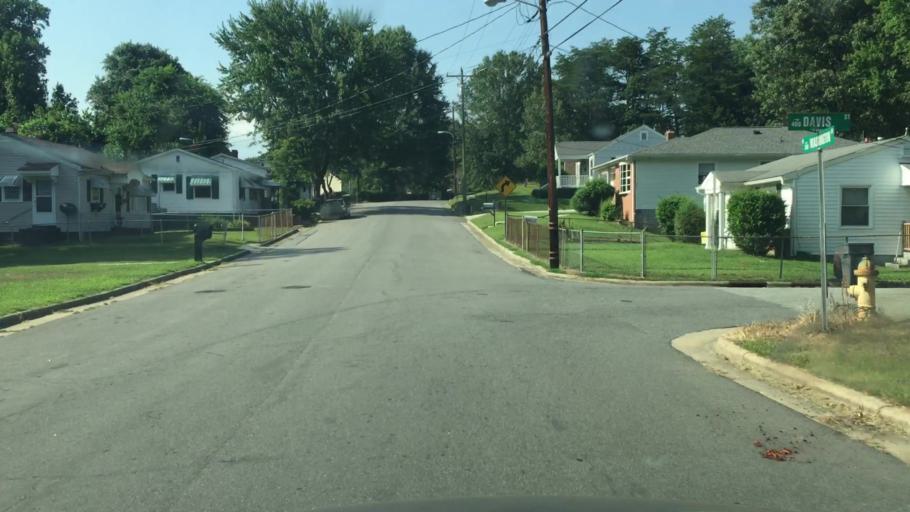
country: US
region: North Carolina
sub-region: Rockingham County
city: Reidsville
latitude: 36.3673
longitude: -79.6714
